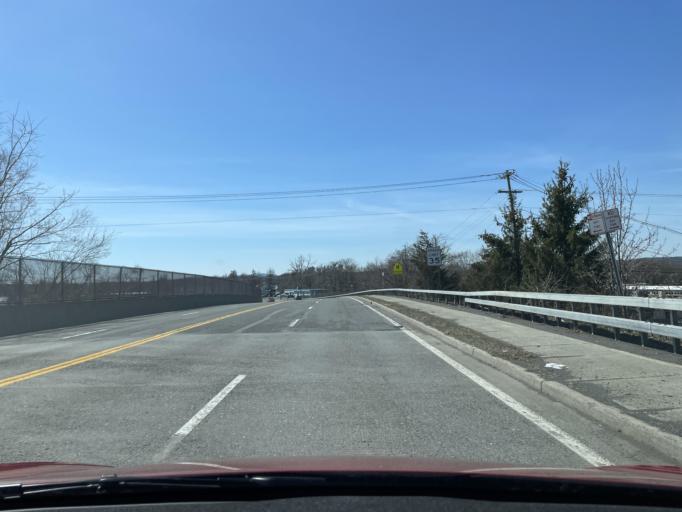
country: US
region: New York
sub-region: Ulster County
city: Lincoln Park
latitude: 41.9590
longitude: -73.9925
